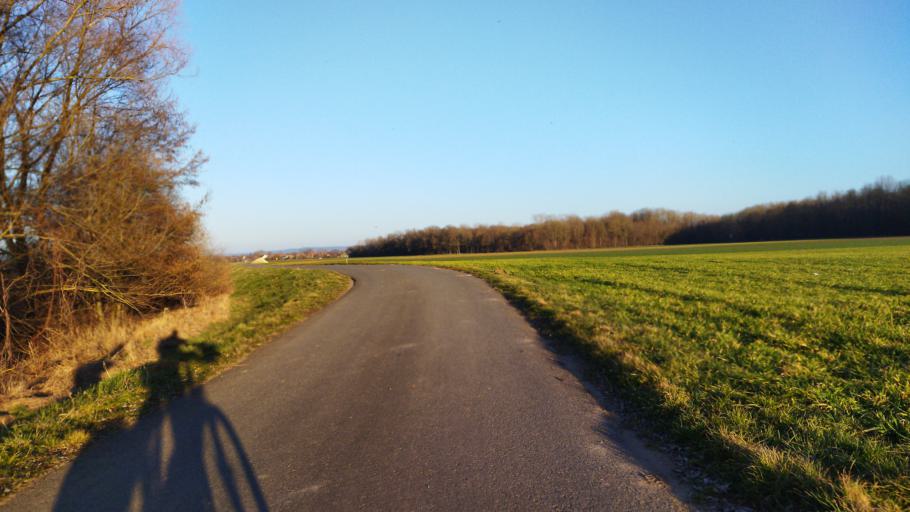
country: DE
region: Bavaria
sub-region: Regierungsbezirk Unterfranken
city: Dettelbach
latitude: 49.7892
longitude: 10.2005
